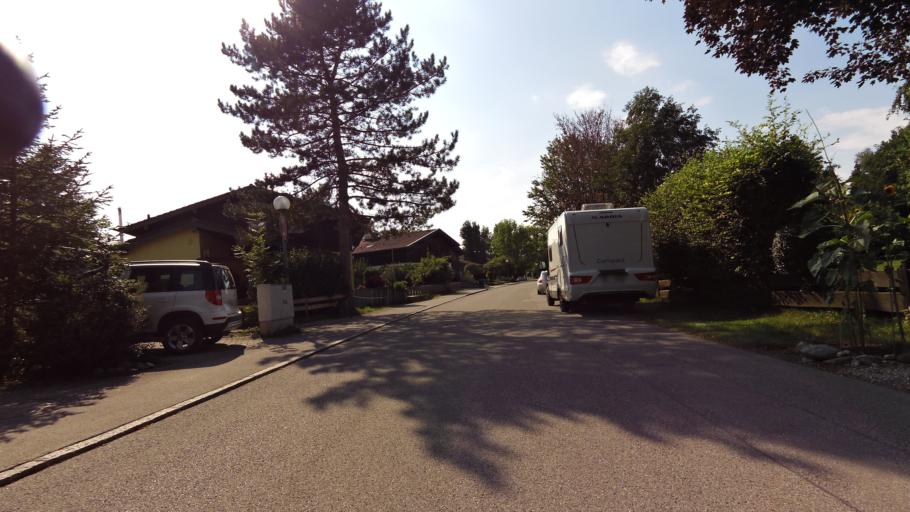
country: DE
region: Bavaria
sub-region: Upper Bavaria
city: Seeon-Seebruck
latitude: 47.9331
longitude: 12.4874
